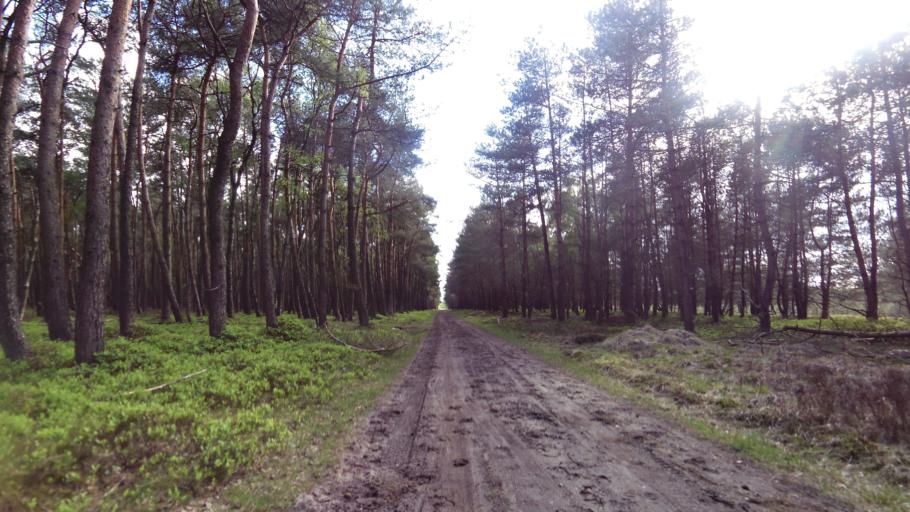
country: NL
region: Gelderland
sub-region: Gemeente Rozendaal
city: Rozendaal
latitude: 52.0686
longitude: 5.9506
